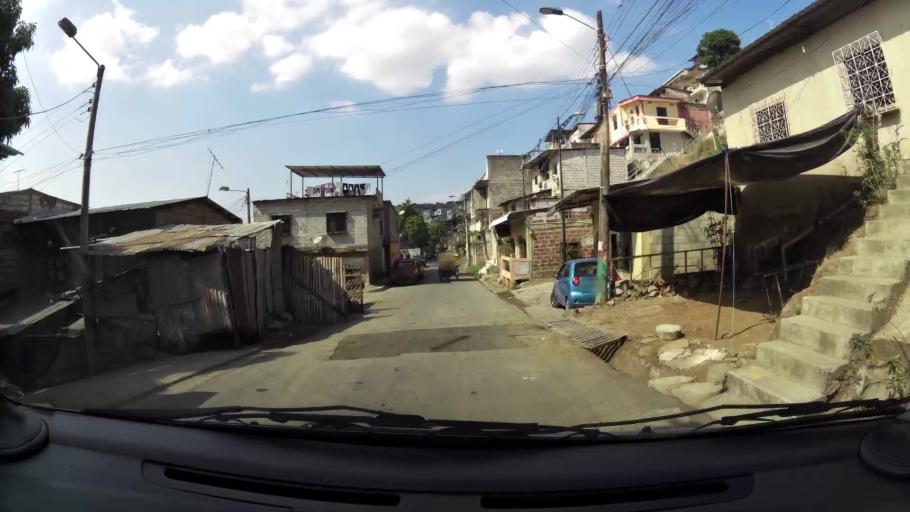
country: EC
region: Guayas
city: Guayaquil
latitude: -2.1509
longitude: -79.9387
